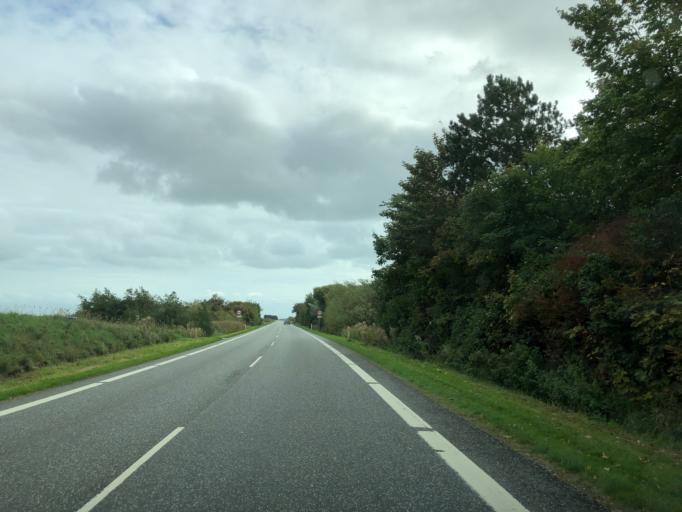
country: DK
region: North Denmark
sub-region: Thisted Kommune
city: Hurup
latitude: 56.6787
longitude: 8.3962
